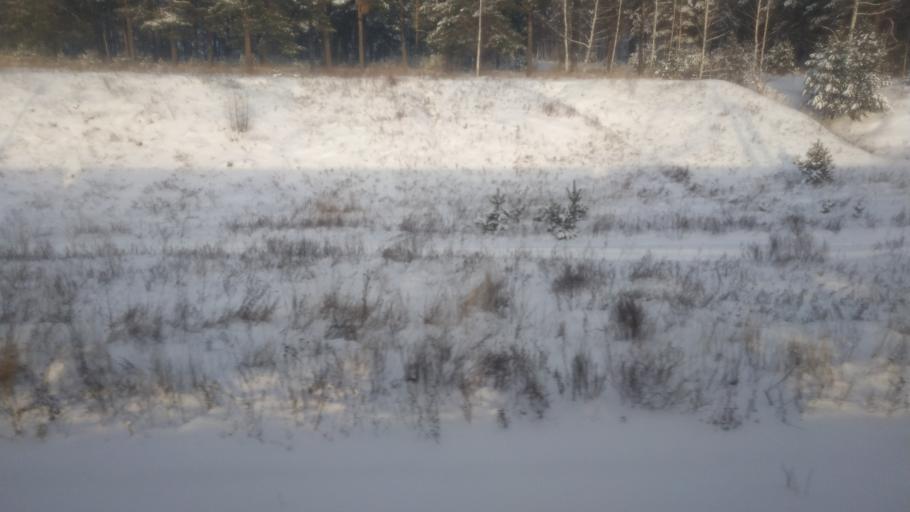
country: RU
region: Kirov
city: Krasnaya Polyana
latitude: 56.2467
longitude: 51.1646
